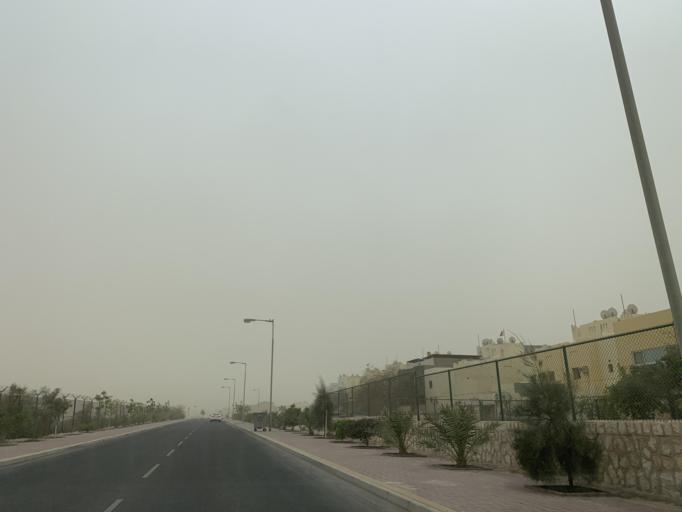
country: BH
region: Central Governorate
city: Madinat Hamad
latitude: 26.1337
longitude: 50.5144
